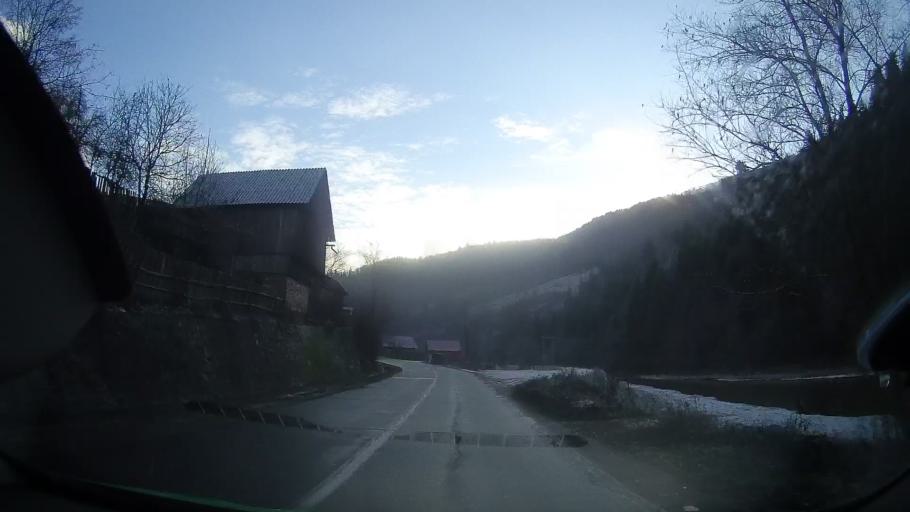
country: RO
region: Alba
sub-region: Comuna Vadu Motilor
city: Vadu Motilor
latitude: 46.3894
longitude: 22.9787
